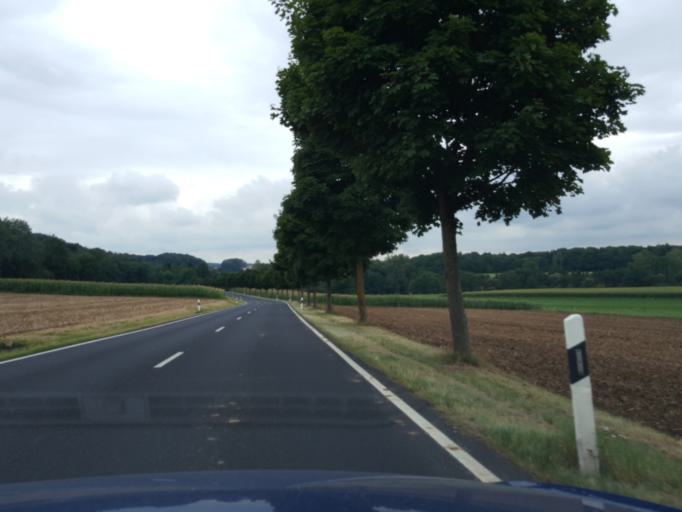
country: LU
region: Luxembourg
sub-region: Canton de Capellen
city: Kehlen
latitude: 49.6552
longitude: 6.0321
